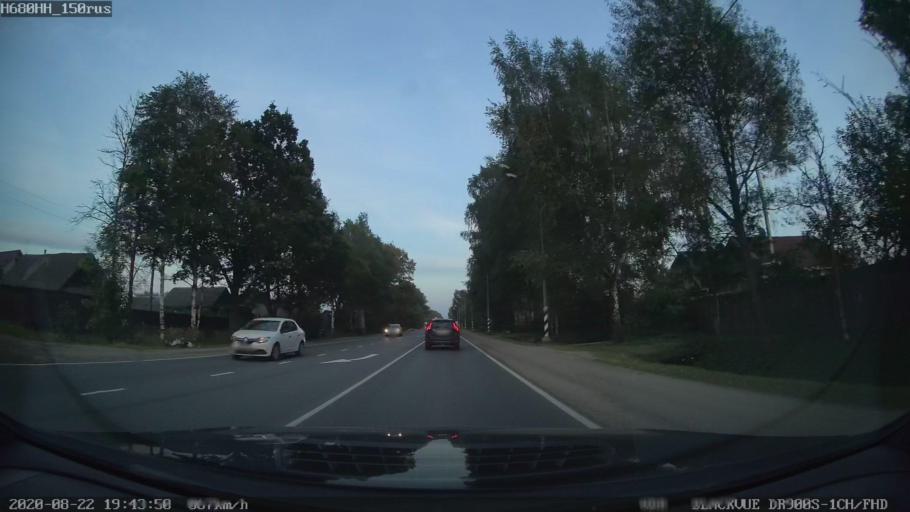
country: RU
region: Tverskaya
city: Emmaus
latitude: 56.7930
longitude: 36.0643
